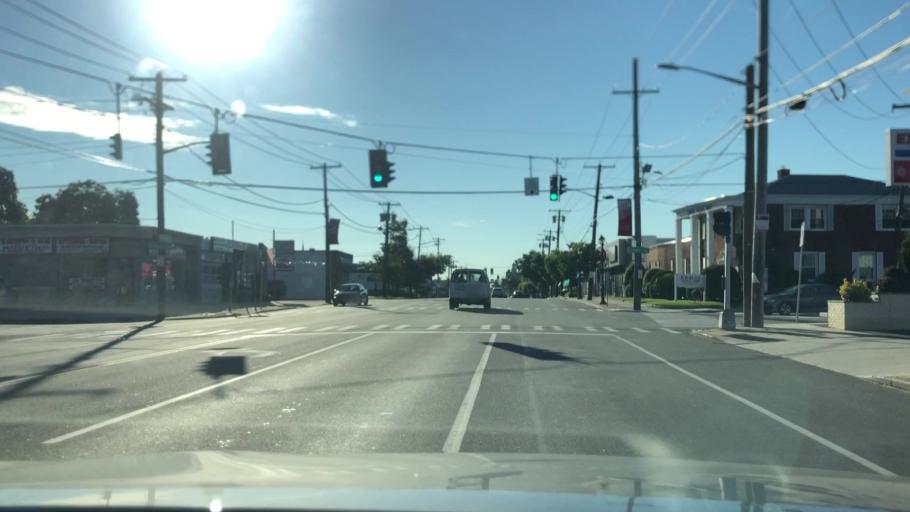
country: US
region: New York
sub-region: Nassau County
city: Franklin Square
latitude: 40.7080
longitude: -73.6812
